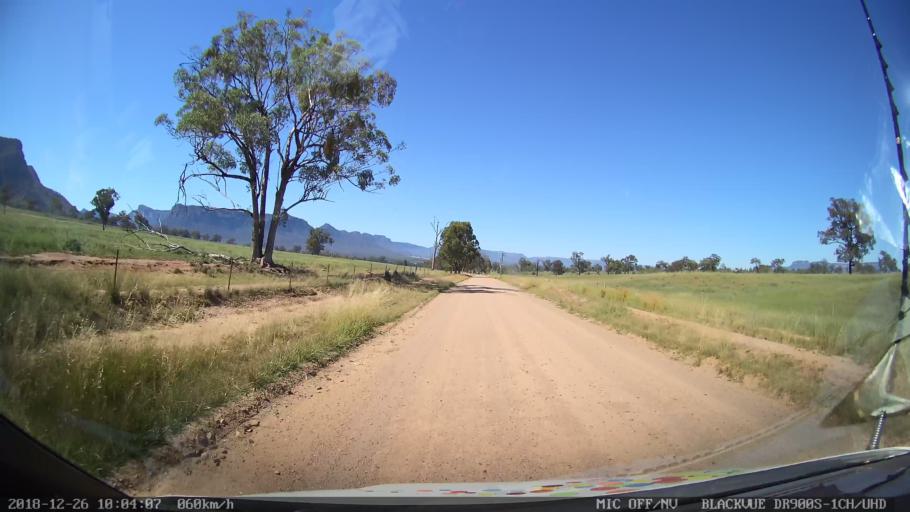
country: AU
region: New South Wales
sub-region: Mid-Western Regional
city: Kandos
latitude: -33.0675
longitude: 150.2157
